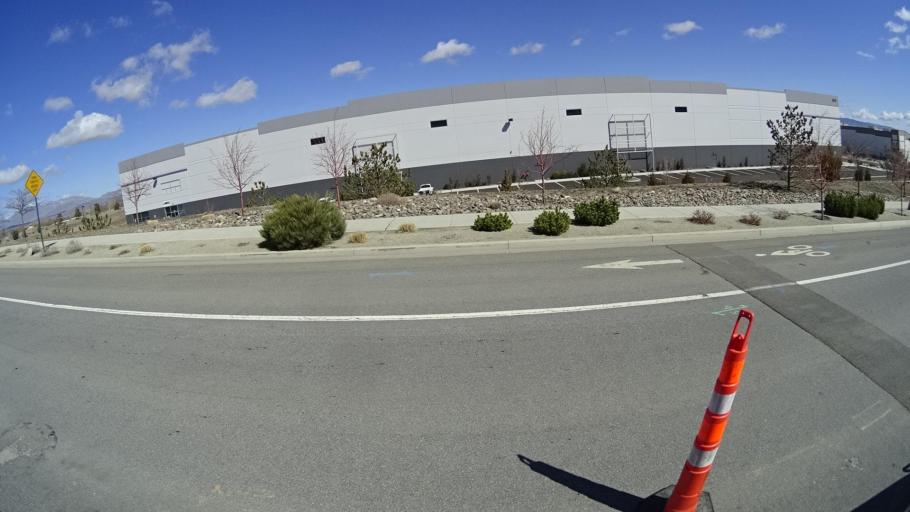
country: US
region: Nevada
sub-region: Washoe County
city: Golden Valley
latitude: 39.6039
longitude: -119.8535
